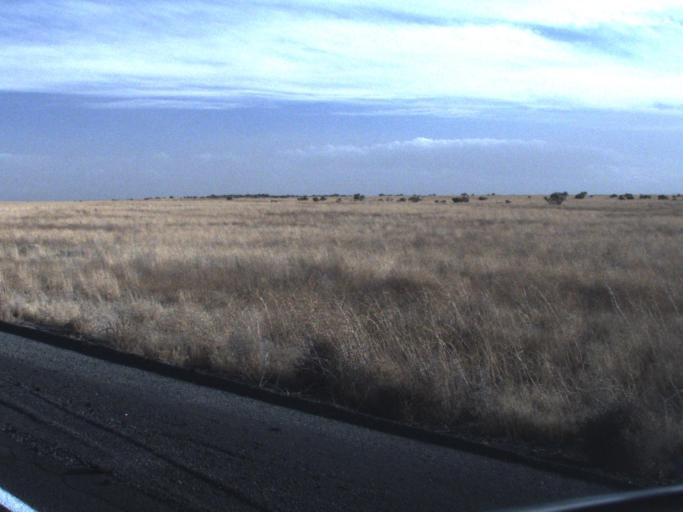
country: US
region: Washington
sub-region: Grant County
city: Moses Lake North
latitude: 47.3648
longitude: -118.9762
